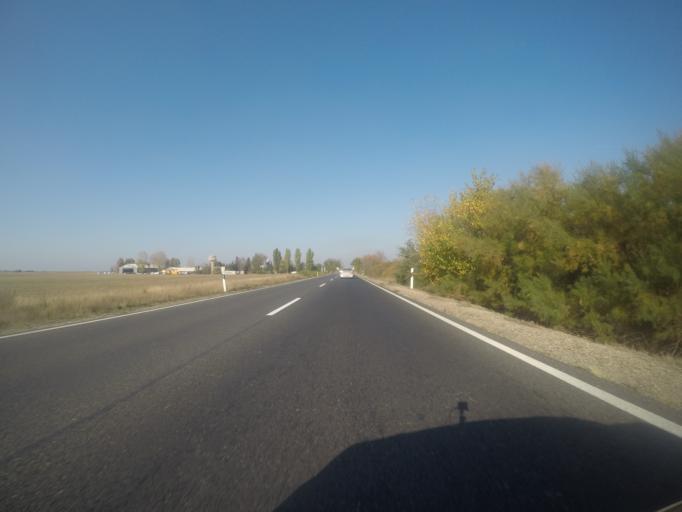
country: HU
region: Fejer
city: Baracs
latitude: 46.8935
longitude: 18.9214
